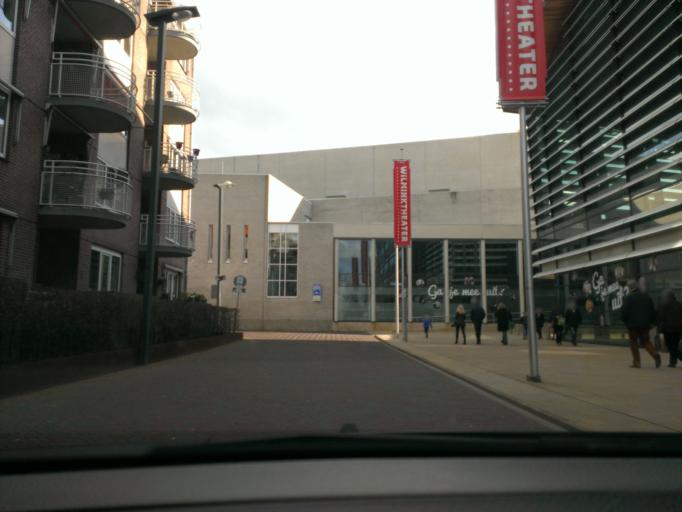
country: NL
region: Overijssel
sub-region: Gemeente Enschede
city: Enschede
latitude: 52.2228
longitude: 6.8958
